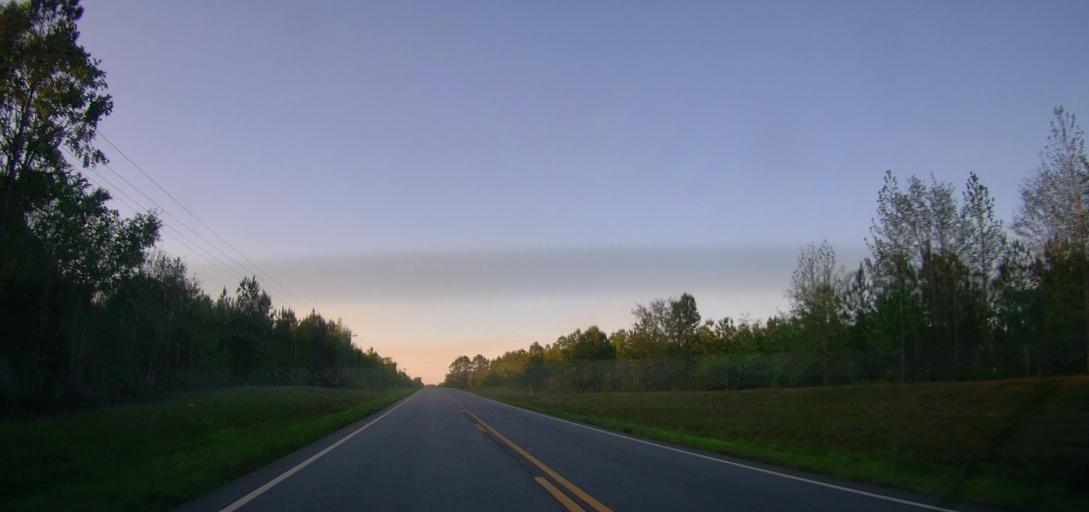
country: US
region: Georgia
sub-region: Talbot County
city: Talbotton
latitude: 32.5600
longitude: -84.5688
